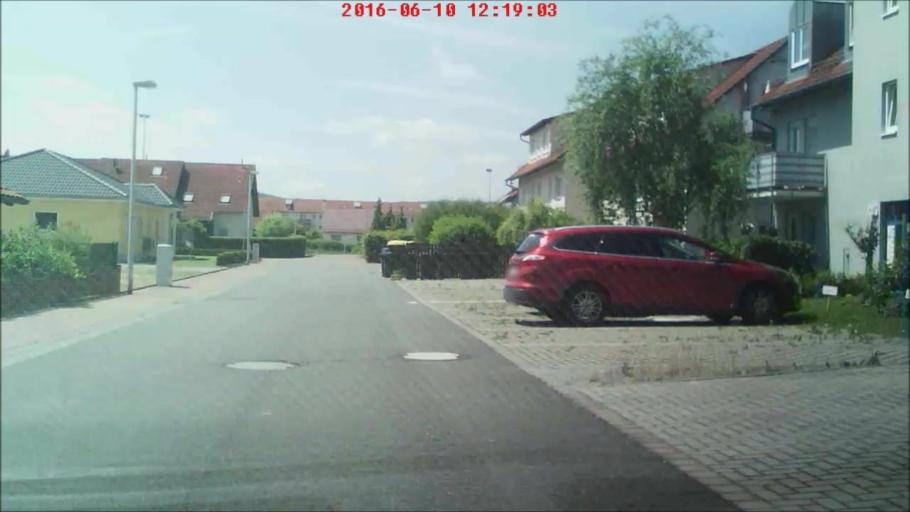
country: DE
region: Thuringia
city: Obermassfeld-Grimmenthal
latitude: 50.5296
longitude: 10.4464
